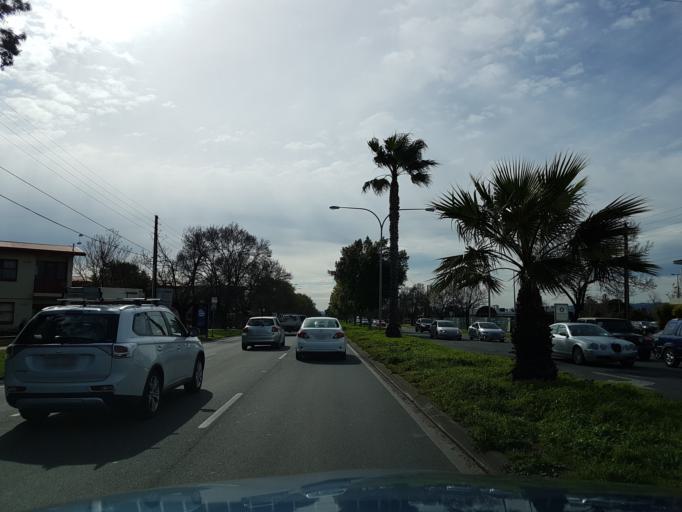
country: AU
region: South Australia
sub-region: Holdfast Bay
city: Glenelg East
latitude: -34.9749
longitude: 138.5379
